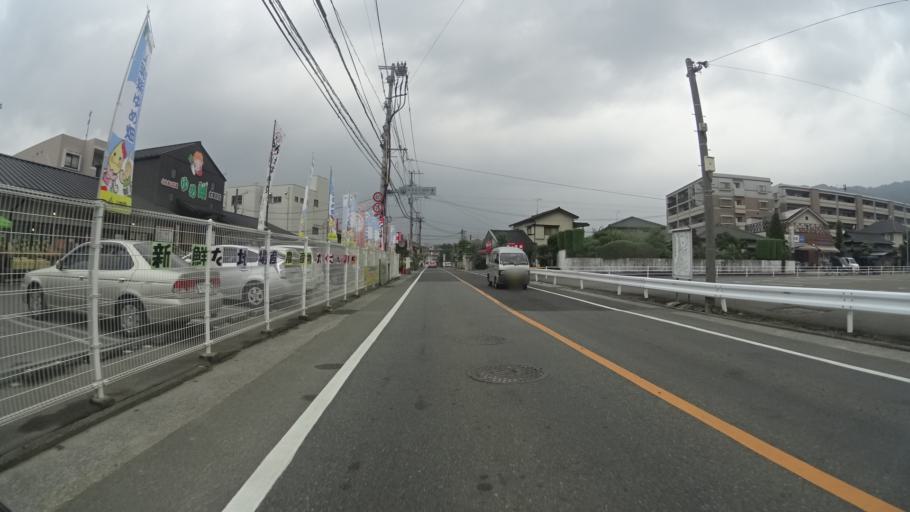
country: JP
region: Fukuoka
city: Dazaifu
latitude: 33.5165
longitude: 130.5317
